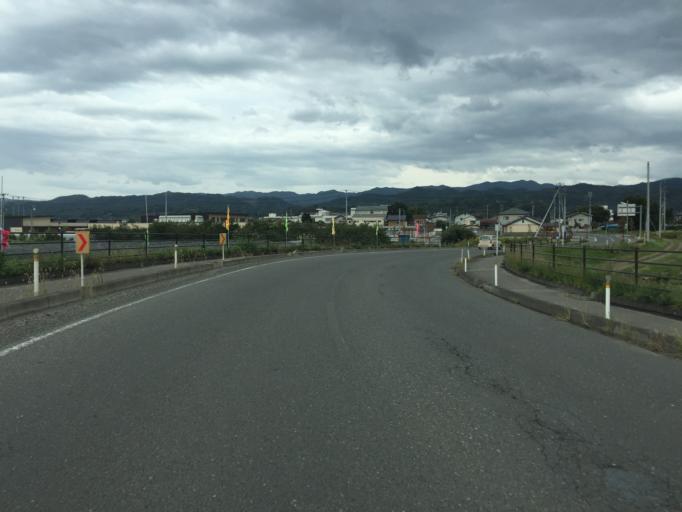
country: JP
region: Fukushima
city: Yanagawamachi-saiwaicho
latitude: 37.8574
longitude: 140.5979
